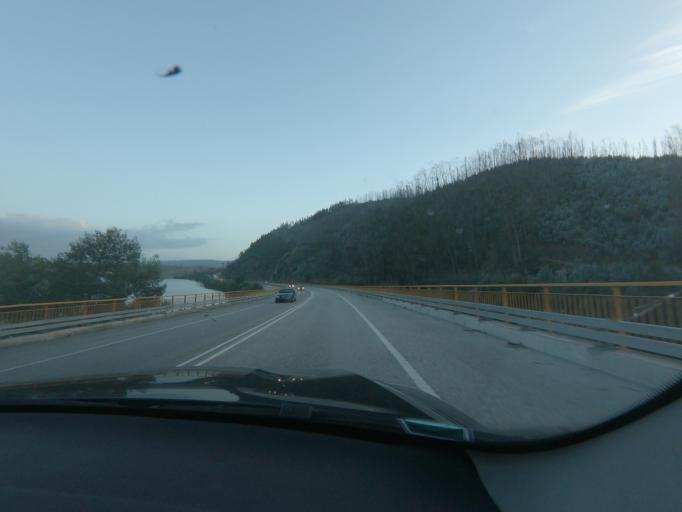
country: PT
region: Viseu
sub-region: Mortagua
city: Mortagua
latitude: 40.3346
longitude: -8.2273
